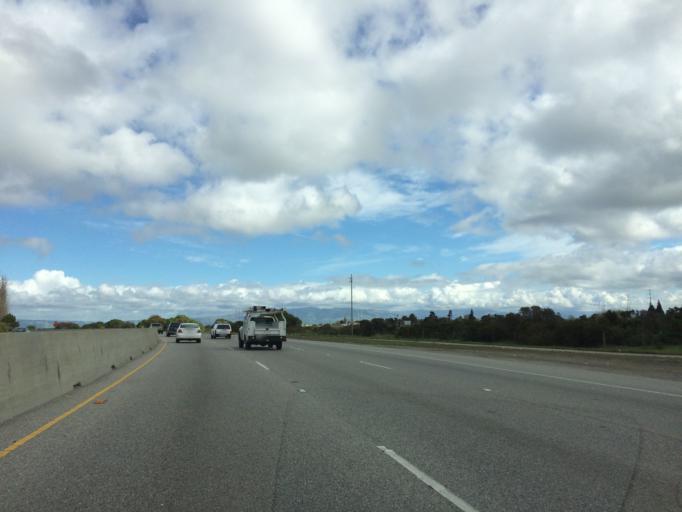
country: US
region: California
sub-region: San Mateo County
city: East Palo Alto
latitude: 37.4822
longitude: -122.1491
